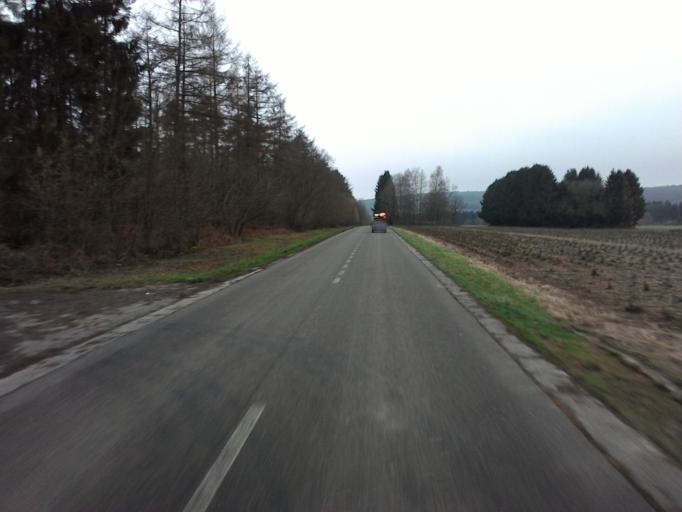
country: BE
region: Wallonia
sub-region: Province de Namur
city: Gedinne
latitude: 50.0379
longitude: 4.9479
